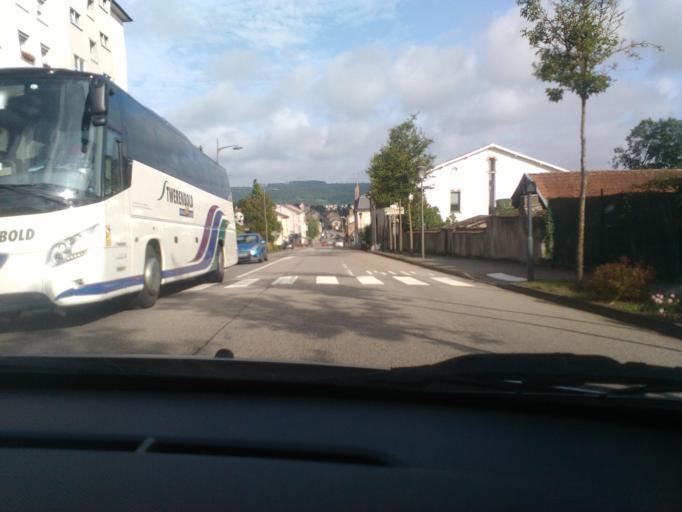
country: FR
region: Lorraine
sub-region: Departement de Meurthe-et-Moselle
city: Frouard
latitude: 48.7539
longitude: 6.1427
